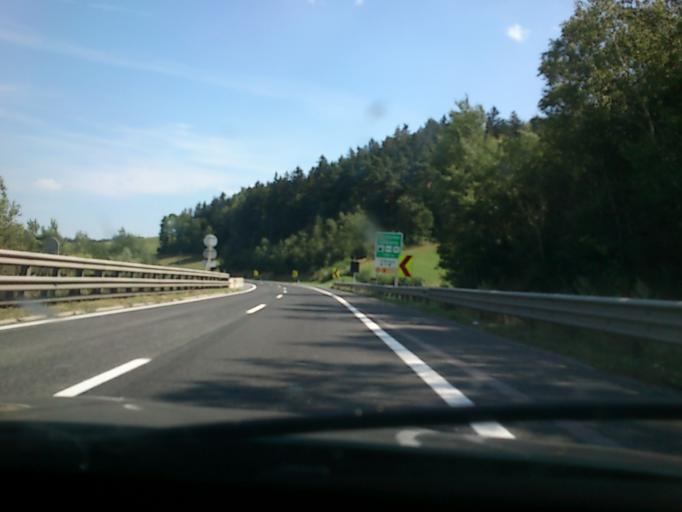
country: AT
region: Lower Austria
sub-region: Politischer Bezirk Neunkirchen
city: Zobern
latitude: 47.5255
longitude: 16.1108
